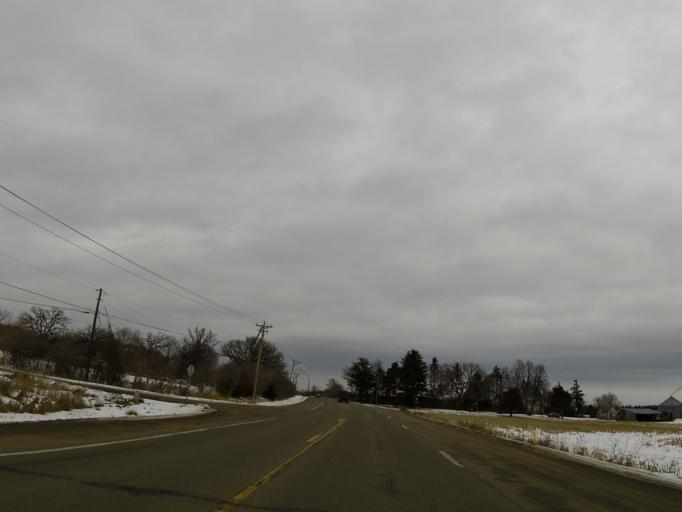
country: US
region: Minnesota
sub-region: Washington County
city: Lakeland
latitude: 44.9754
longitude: -92.7925
